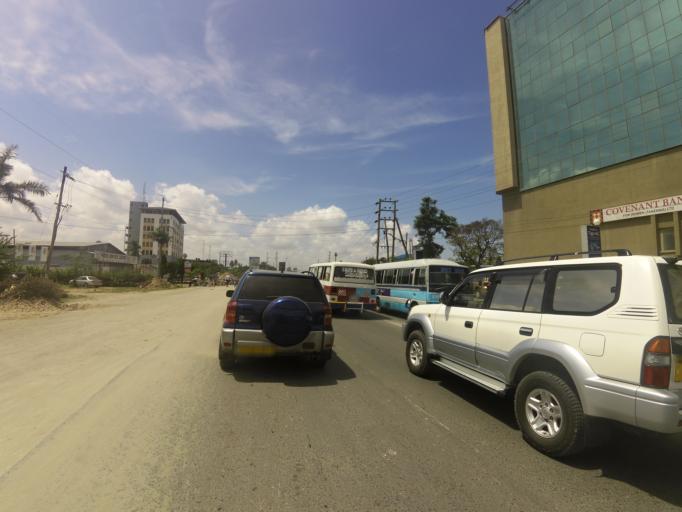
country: TZ
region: Dar es Salaam
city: Magomeni
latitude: -6.7756
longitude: 39.2439
